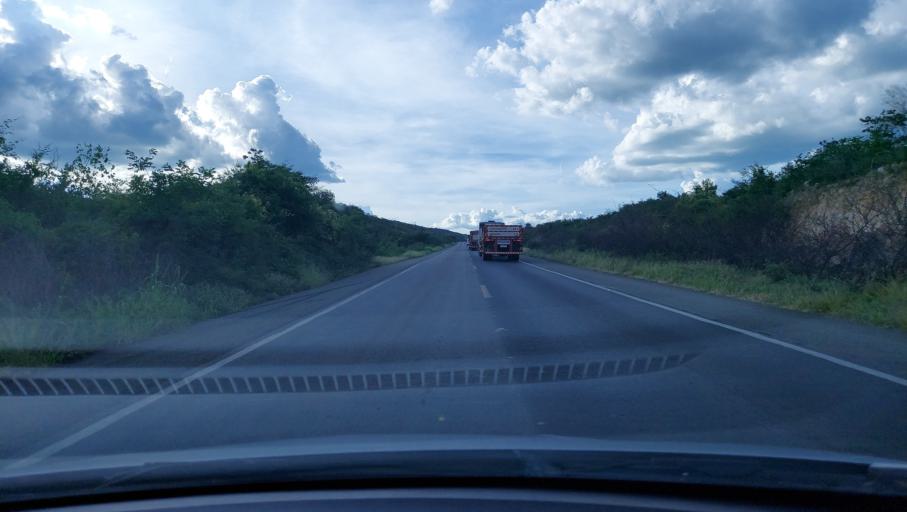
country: BR
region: Bahia
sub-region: Oliveira Dos Brejinhos
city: Beira Rio
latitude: -12.4418
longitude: -42.3381
